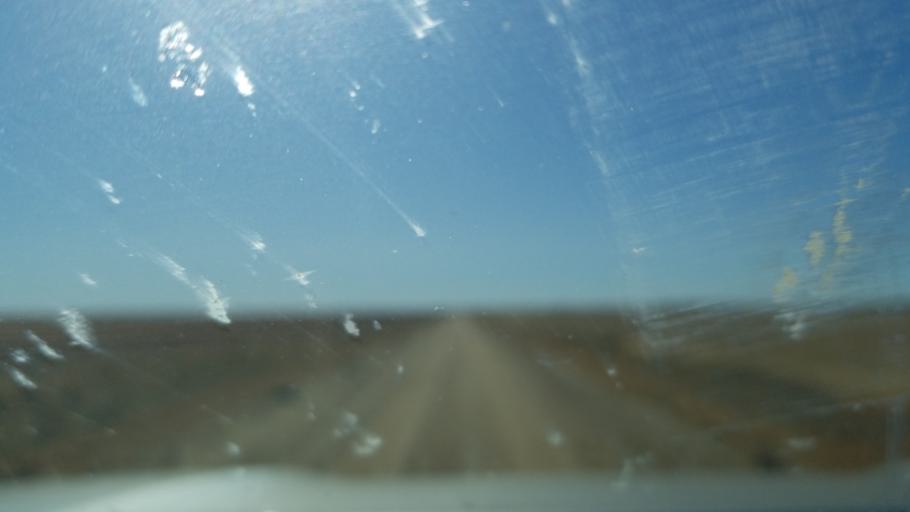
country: US
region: Kansas
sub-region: Ness County
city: Ness City
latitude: 38.5744
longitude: -99.6420
